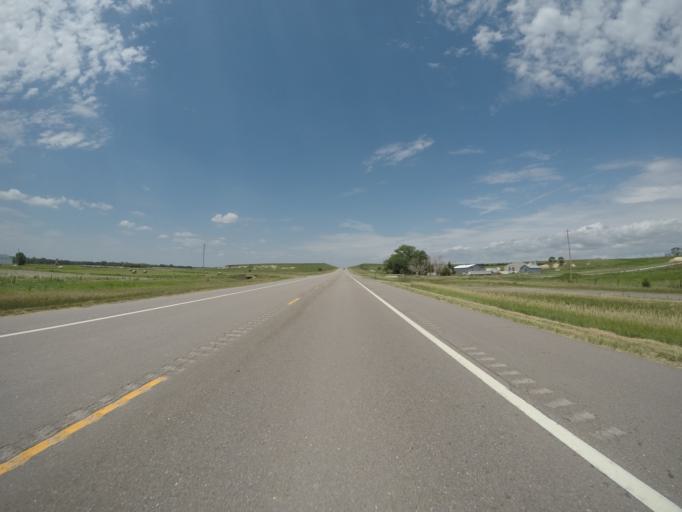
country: US
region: Kansas
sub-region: Graham County
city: Hill City
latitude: 39.3795
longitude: -99.6952
